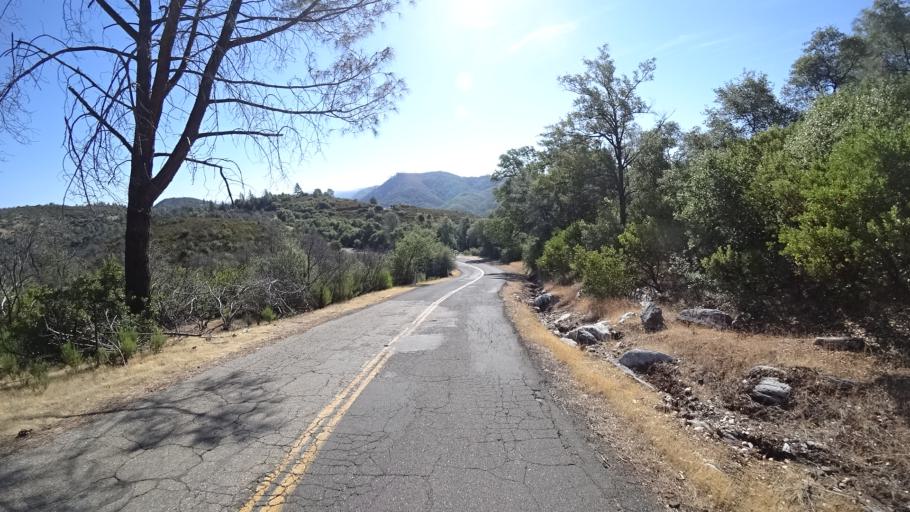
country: US
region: California
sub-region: Calaveras County
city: Mountain Ranch
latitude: 38.1643
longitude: -120.5475
